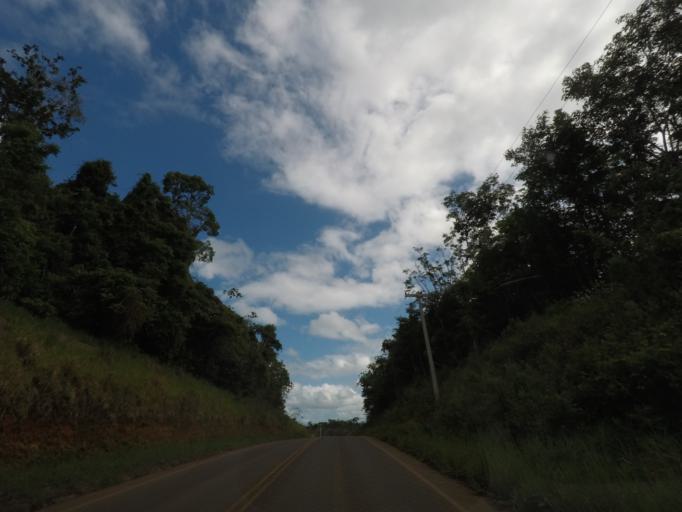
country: BR
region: Bahia
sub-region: Itacare
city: Itacare
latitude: -14.2187
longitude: -39.0992
